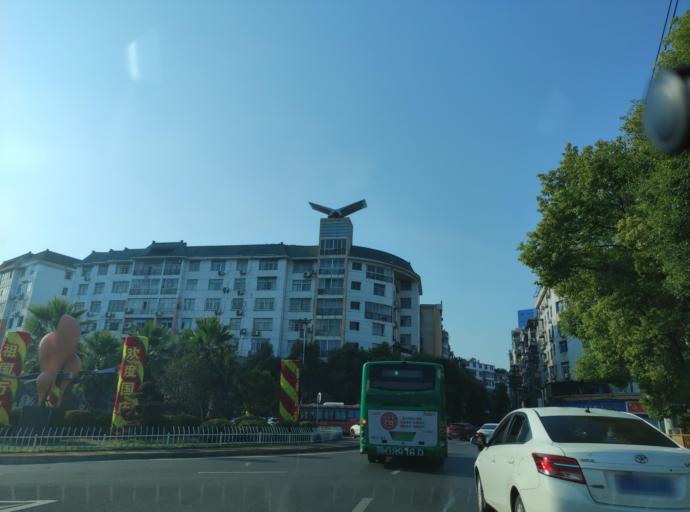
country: CN
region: Jiangxi Sheng
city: Pingxiang
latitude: 27.6292
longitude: 113.8507
